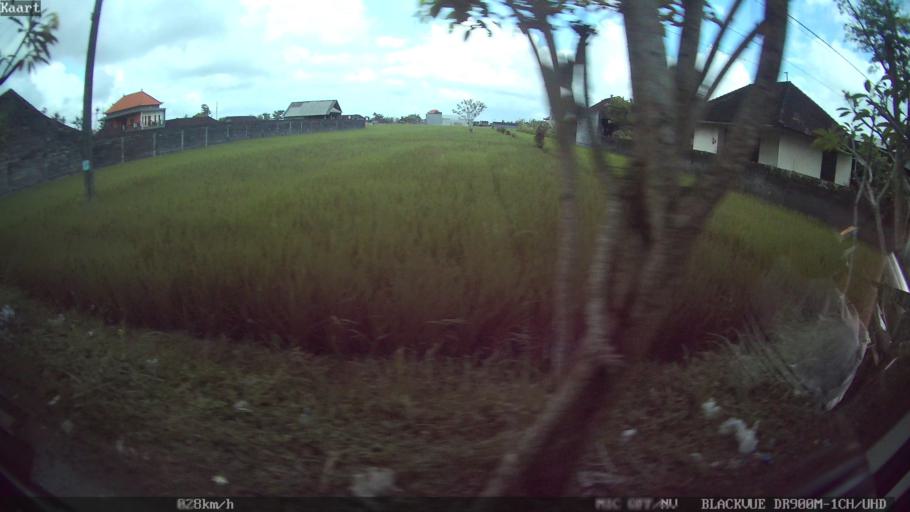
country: ID
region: Bali
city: Banjar Bucu
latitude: -8.5774
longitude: 115.2034
